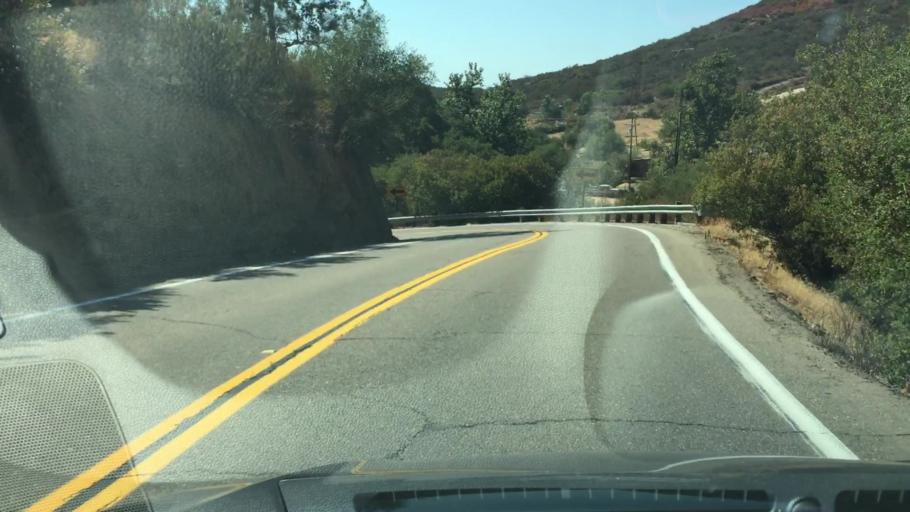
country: US
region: California
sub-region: San Diego County
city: Alpine
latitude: 32.7538
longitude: -116.7771
